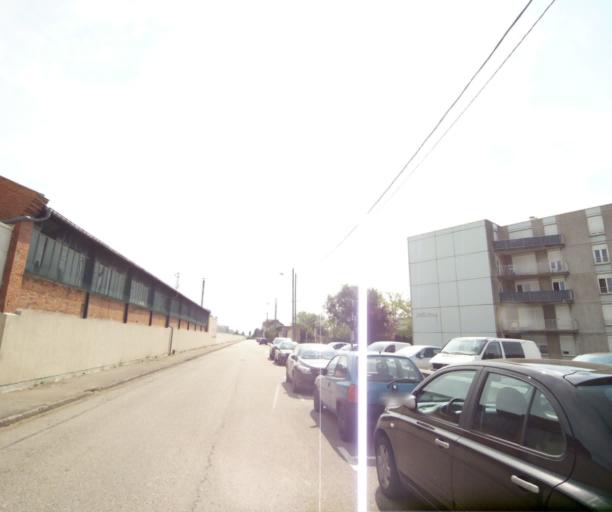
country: FR
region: Lorraine
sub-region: Departement de Meurthe-et-Moselle
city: Luneville
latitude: 48.5897
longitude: 6.5114
